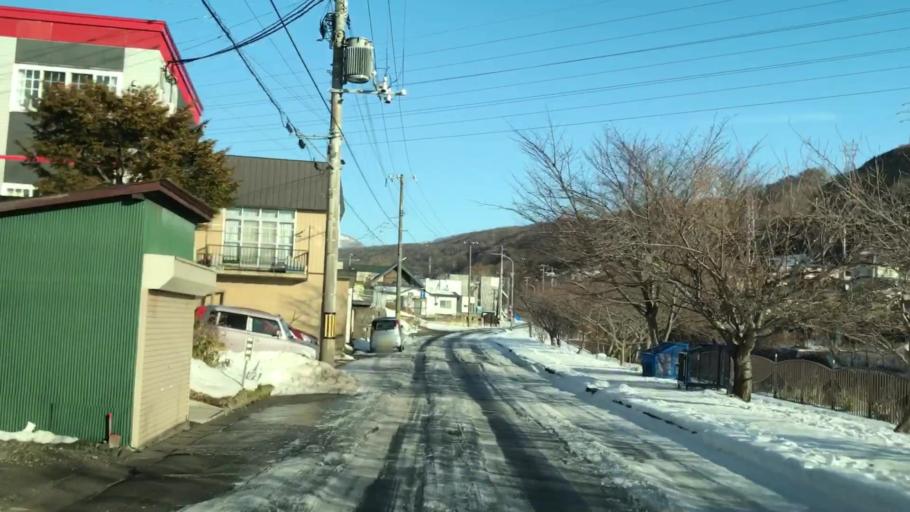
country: JP
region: Hokkaido
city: Muroran
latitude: 42.3705
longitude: 141.0376
